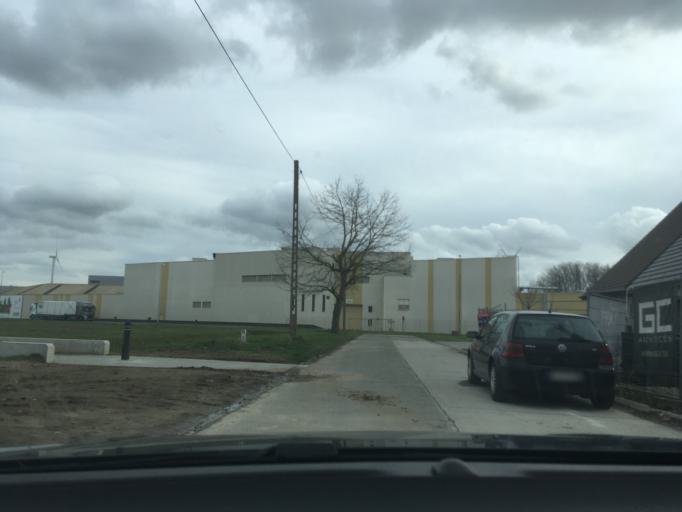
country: BE
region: Flanders
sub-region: Provincie West-Vlaanderen
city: Wielsbeke
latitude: 50.9059
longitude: 3.3666
